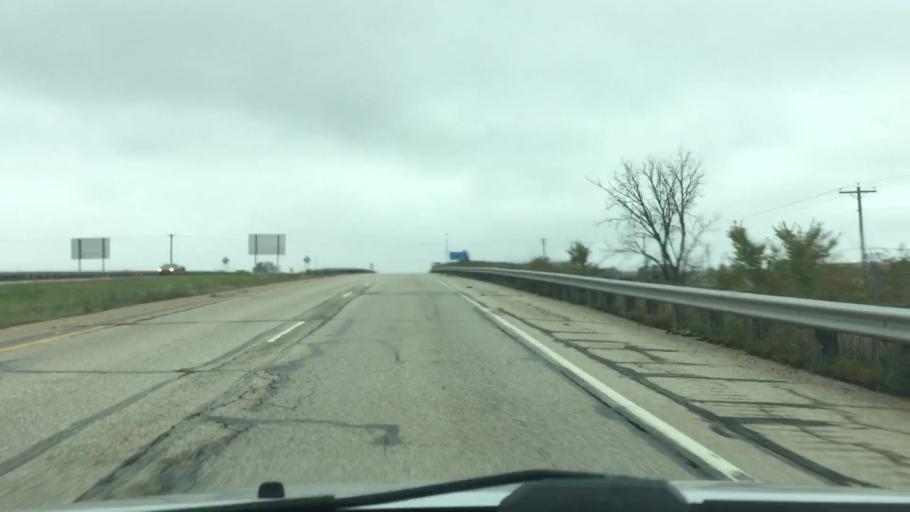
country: US
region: Wisconsin
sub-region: Walworth County
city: Elkhorn
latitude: 42.6846
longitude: -88.5293
